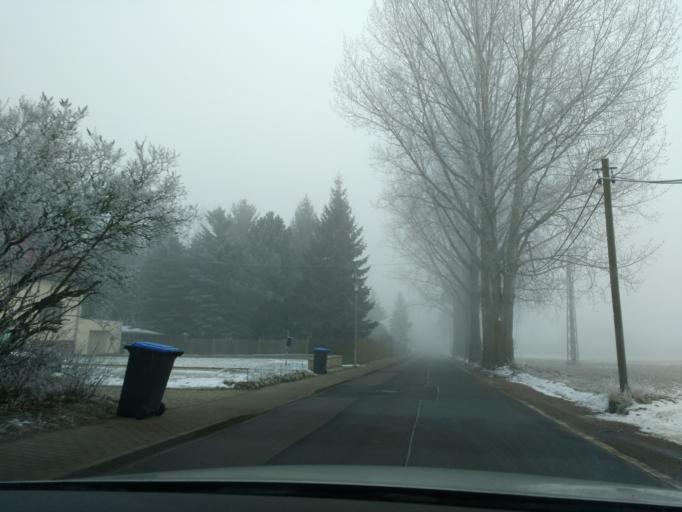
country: DE
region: Saxony-Anhalt
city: Oppin
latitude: 51.5532
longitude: 12.0224
